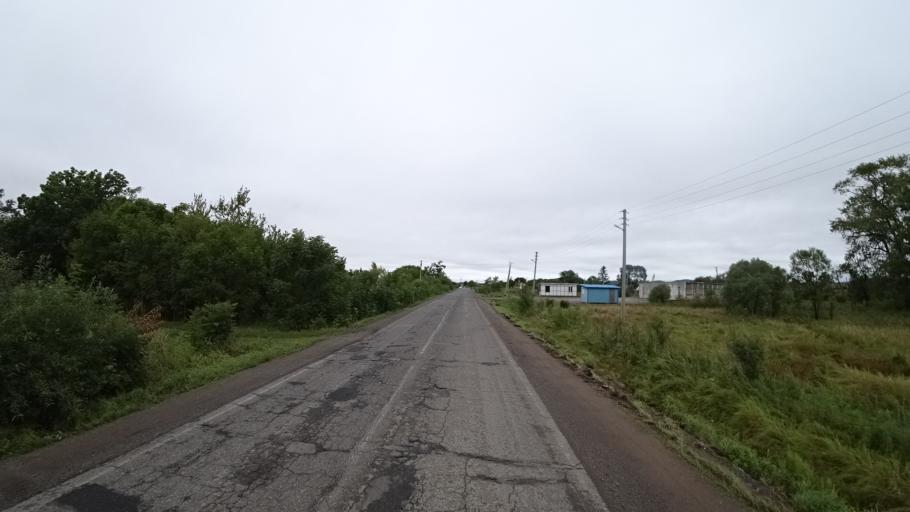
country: RU
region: Primorskiy
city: Monastyrishche
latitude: 44.1910
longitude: 132.4813
